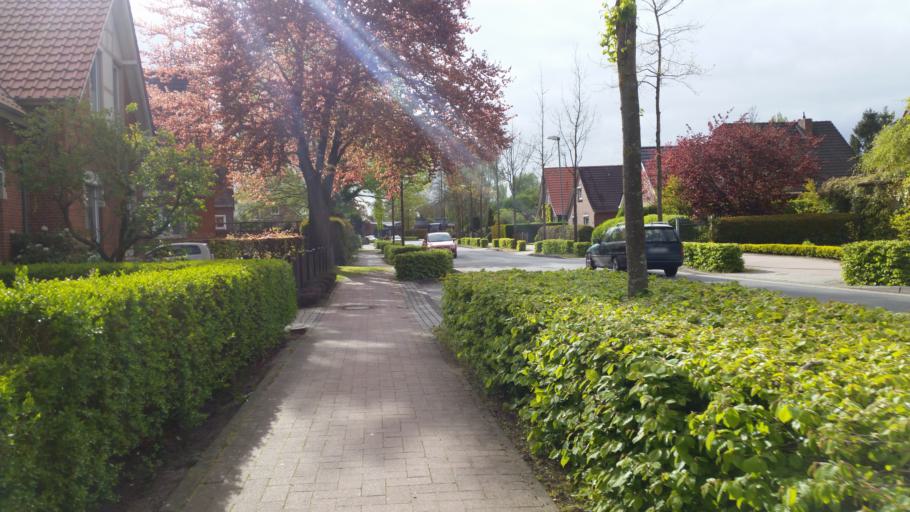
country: DE
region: Lower Saxony
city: Aurich
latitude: 53.4743
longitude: 7.4740
